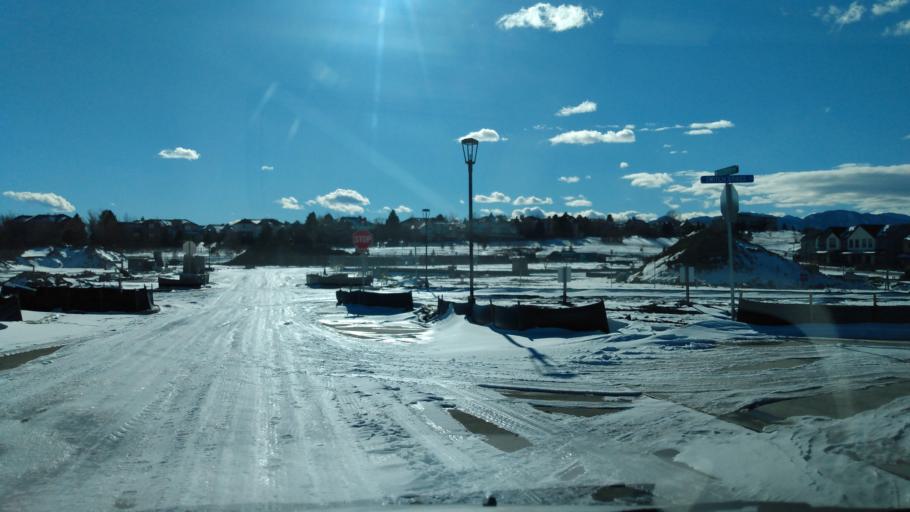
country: US
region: Colorado
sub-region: Boulder County
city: Superior
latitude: 39.9487
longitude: -105.1566
